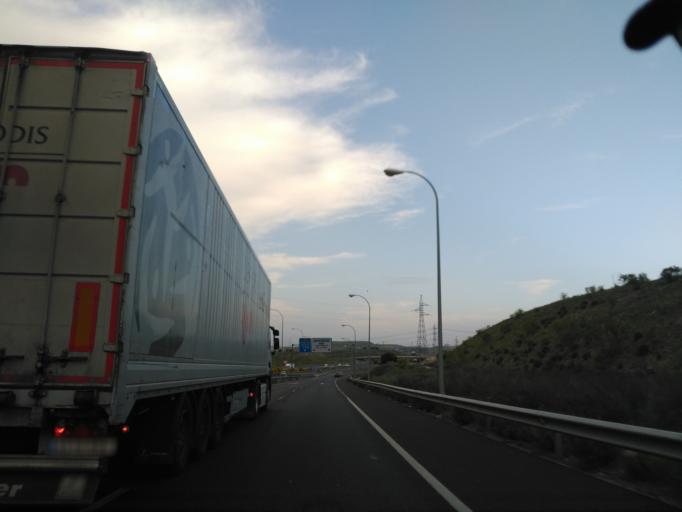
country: ES
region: Madrid
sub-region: Provincia de Madrid
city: Villaverde
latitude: 40.3298
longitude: -3.6793
